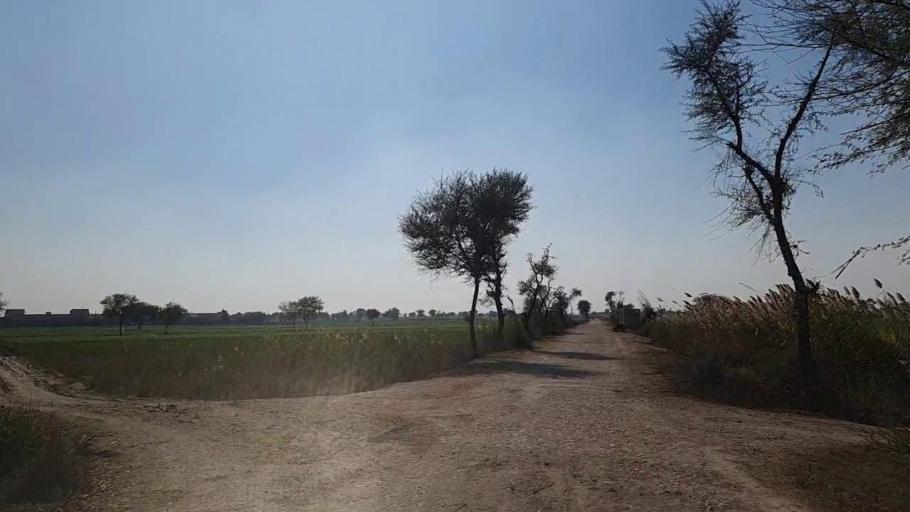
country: PK
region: Sindh
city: Bandhi
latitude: 26.5247
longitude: 68.2904
